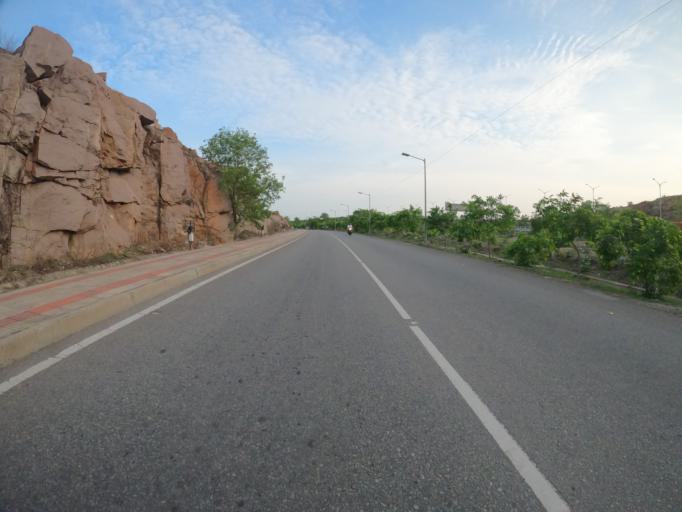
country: IN
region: Telangana
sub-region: Hyderabad
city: Hyderabad
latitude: 17.3755
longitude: 78.3494
